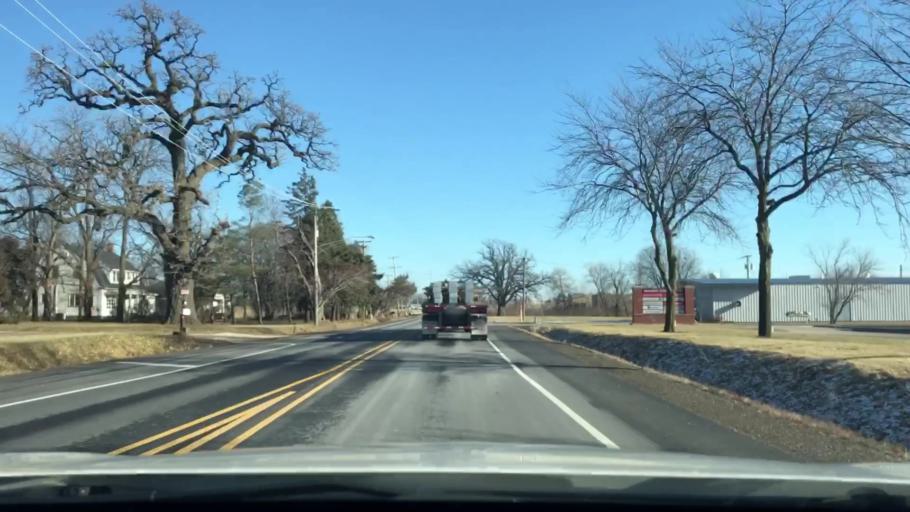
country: US
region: Illinois
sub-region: Kane County
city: Gilberts
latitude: 42.1033
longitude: -88.3667
